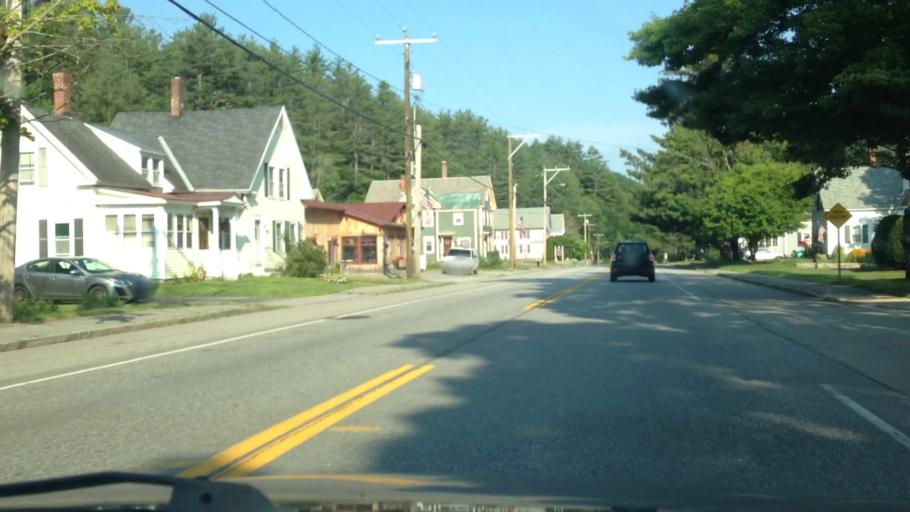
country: US
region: New Hampshire
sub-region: Cheshire County
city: Marlborough
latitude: 42.9075
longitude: -72.2130
